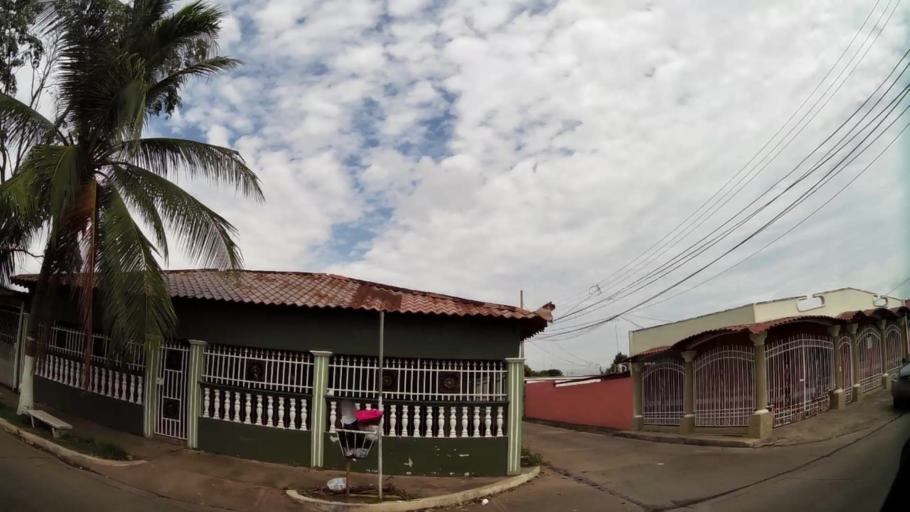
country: PA
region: Panama
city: Tocumen
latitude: 9.0486
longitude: -79.4129
